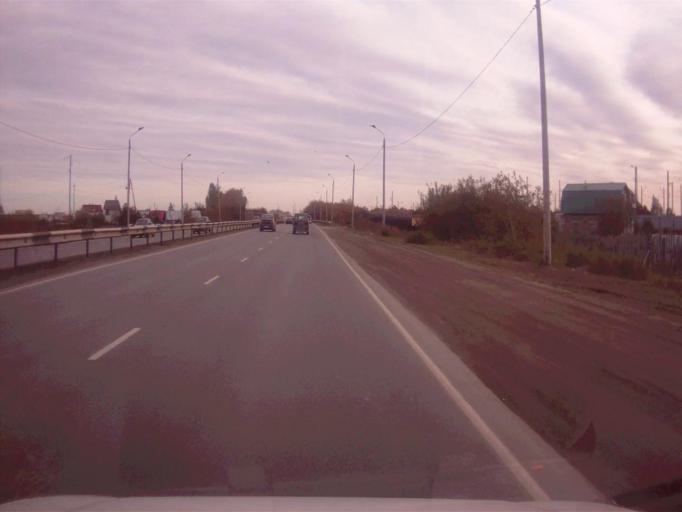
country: RU
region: Chelyabinsk
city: Novosineglazovskiy
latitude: 55.0447
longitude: 61.4217
